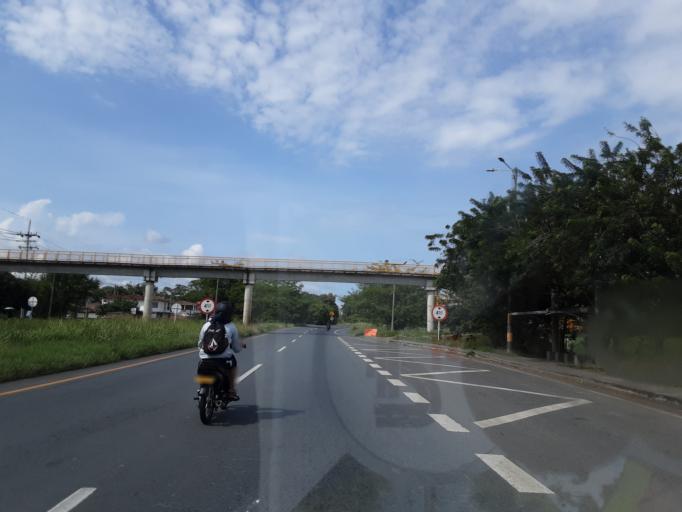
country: CO
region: Valle del Cauca
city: Guacari
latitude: 3.8180
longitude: -76.3068
